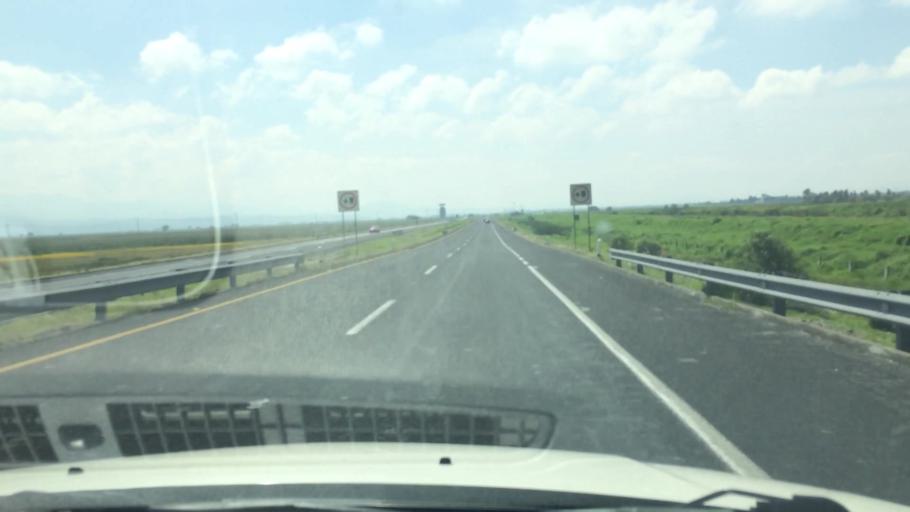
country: MX
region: Mexico
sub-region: Toluca
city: La Constitucion Toltepec
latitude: 19.3597
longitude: -99.5362
